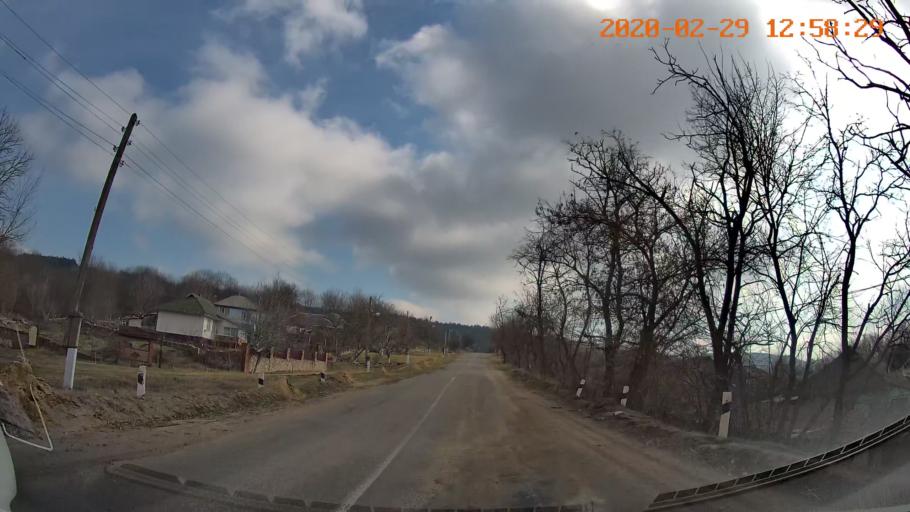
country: MD
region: Telenesti
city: Camenca
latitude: 48.0700
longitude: 28.7213
